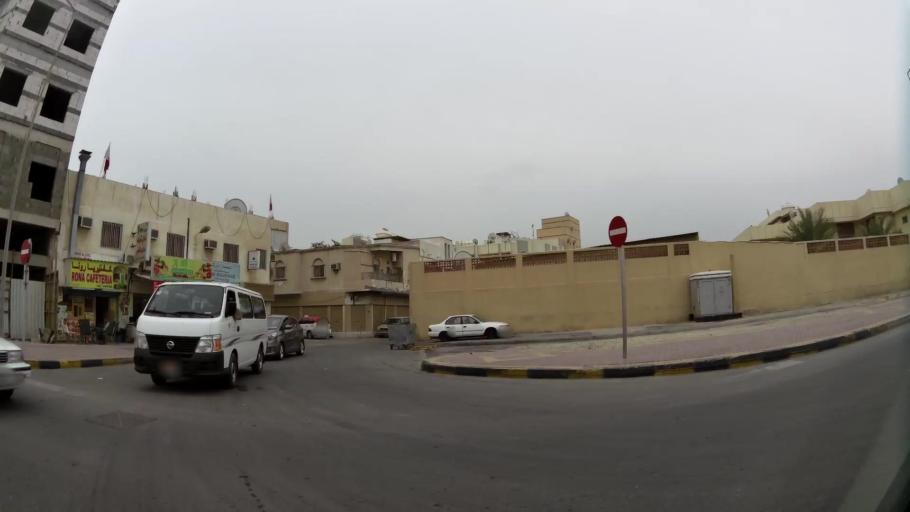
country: BH
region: Manama
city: Jidd Hafs
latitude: 26.2275
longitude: 50.5651
